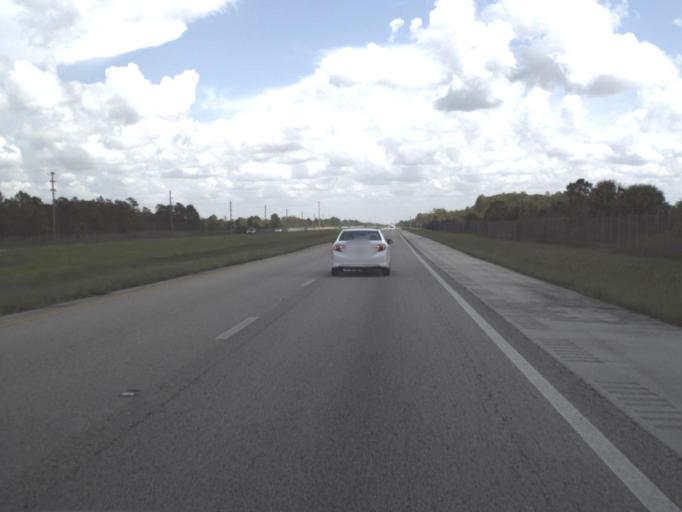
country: US
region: Florida
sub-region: Collier County
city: Immokalee
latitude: 26.1701
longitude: -80.9927
